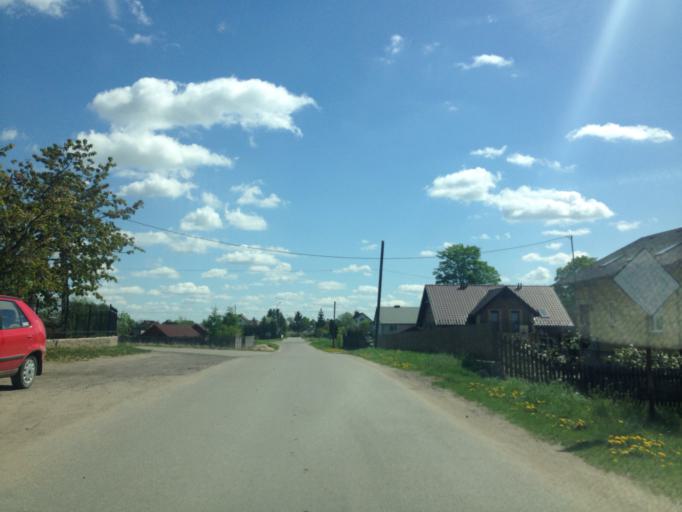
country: PL
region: Kujawsko-Pomorskie
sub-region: Powiat brodnicki
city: Brzozie
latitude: 53.3213
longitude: 19.6049
